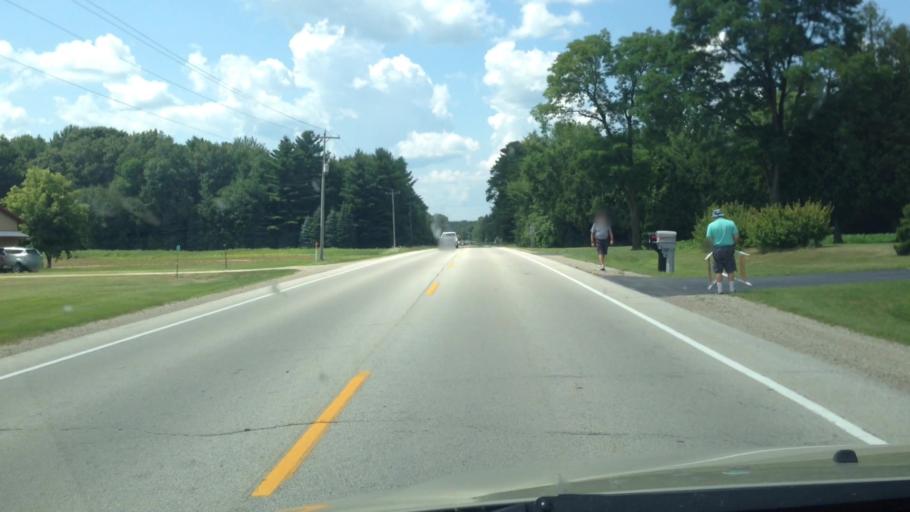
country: US
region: Wisconsin
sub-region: Brown County
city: Suamico
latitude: 44.6429
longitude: -88.0852
